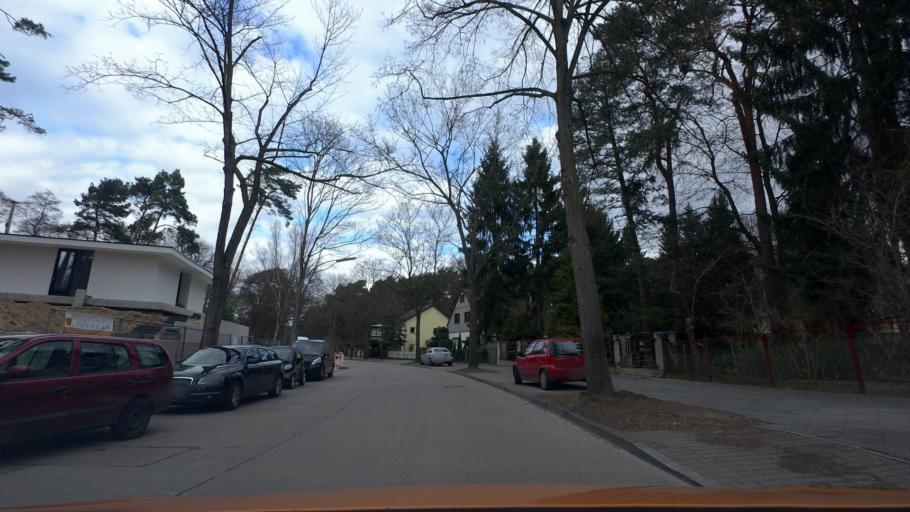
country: DE
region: Berlin
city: Konradshohe
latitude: 52.5915
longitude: 13.2242
